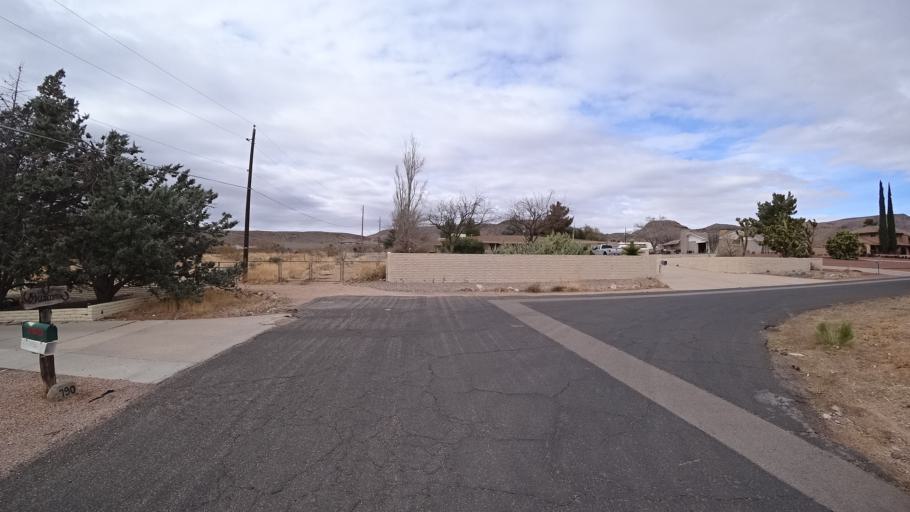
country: US
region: Arizona
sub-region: Mohave County
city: New Kingman-Butler
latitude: 35.2341
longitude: -114.0479
